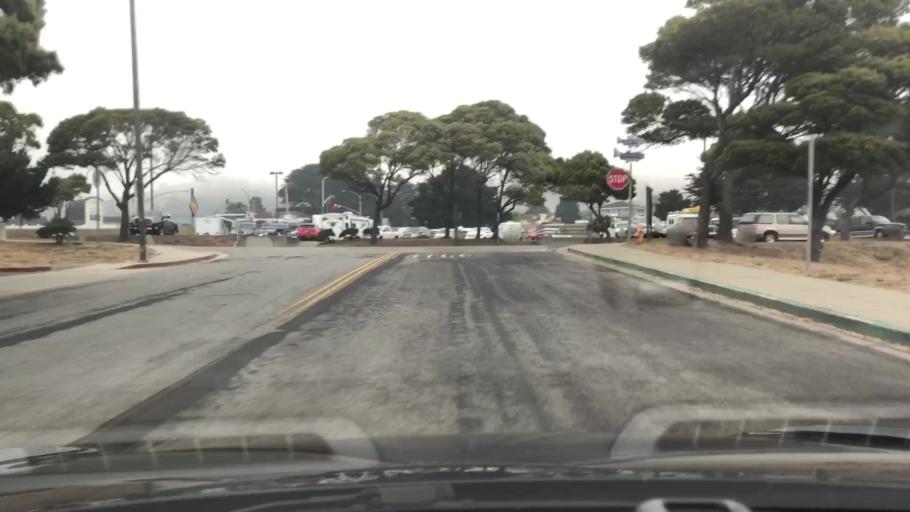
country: US
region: California
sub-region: San Mateo County
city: El Granada
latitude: 37.5034
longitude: -122.4820
